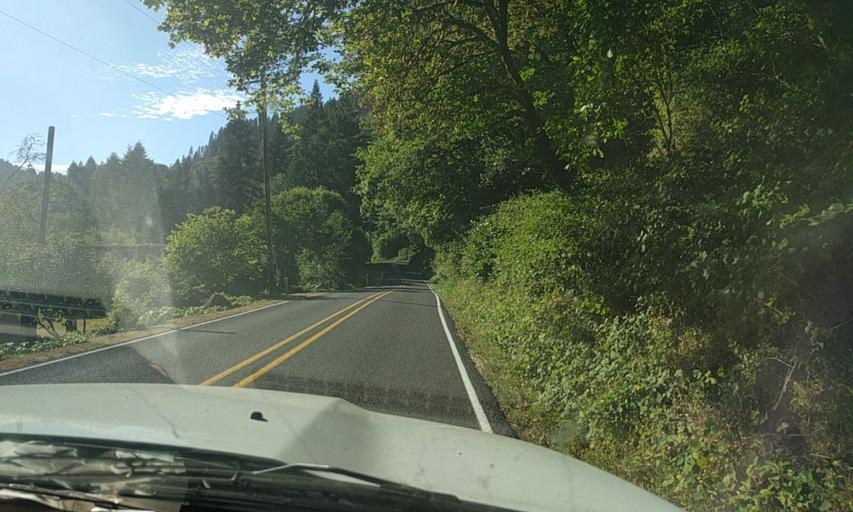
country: US
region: Oregon
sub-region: Lane County
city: Florence
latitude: 44.0401
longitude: -123.8637
